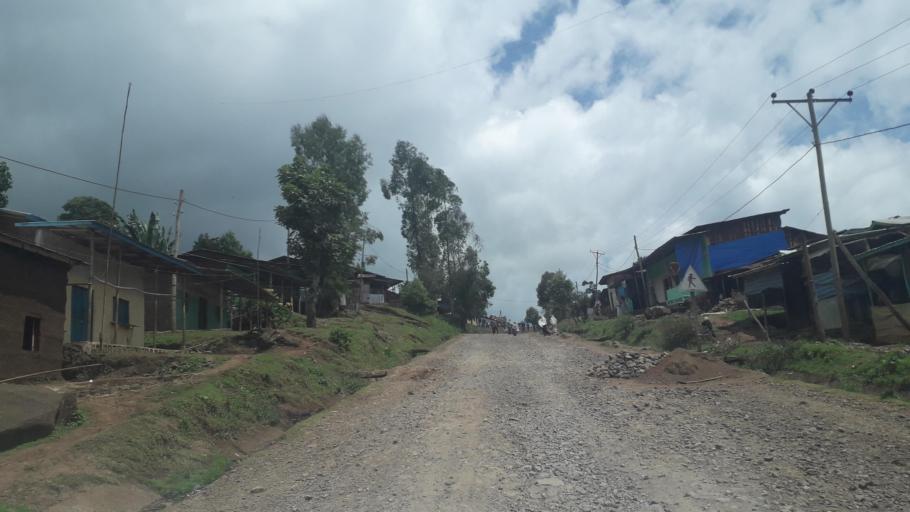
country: ET
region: Oromiya
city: Jima
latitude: 7.4201
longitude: 36.8705
